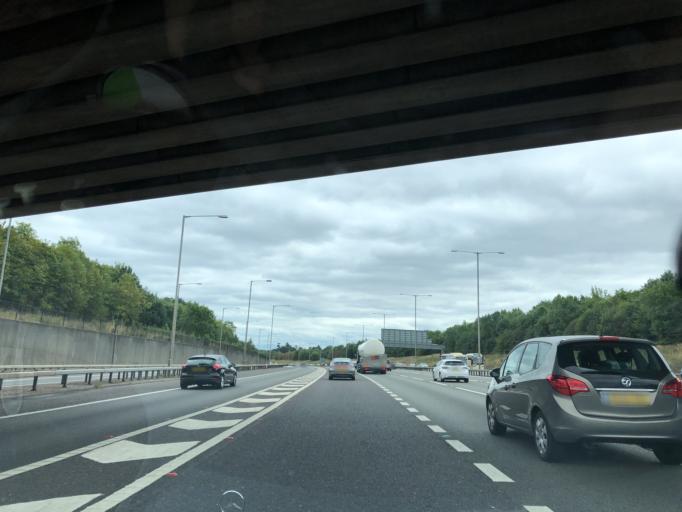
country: GB
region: England
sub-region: Buckinghamshire
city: Denham
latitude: 51.5529
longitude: -0.5257
